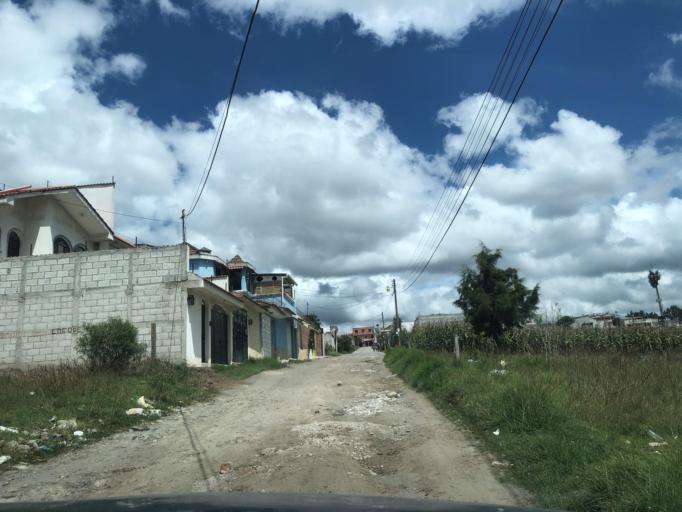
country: GT
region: Quetzaltenango
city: Quetzaltenango
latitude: 14.8392
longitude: -91.5444
